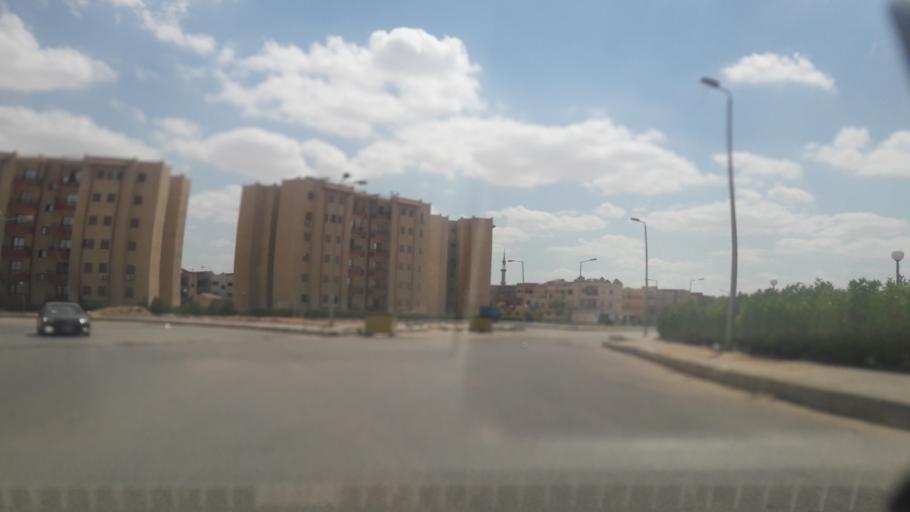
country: EG
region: Al Jizah
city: Madinat Sittah Uktubar
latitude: 29.9351
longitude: 31.0652
